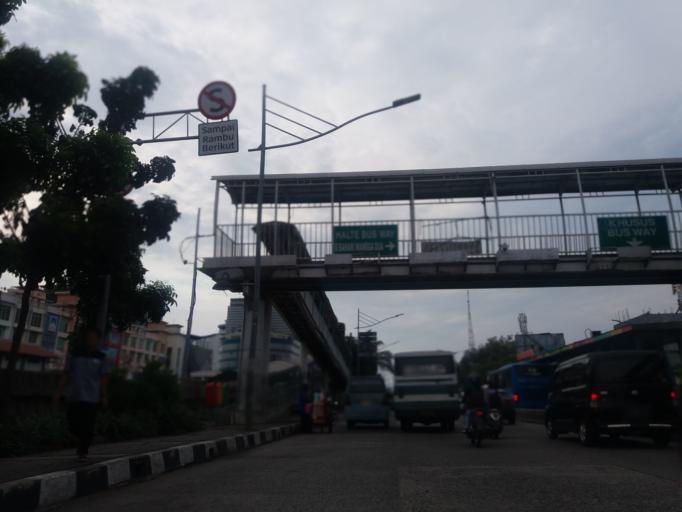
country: ID
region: Jakarta Raya
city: Jakarta
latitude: -6.1372
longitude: 106.8323
